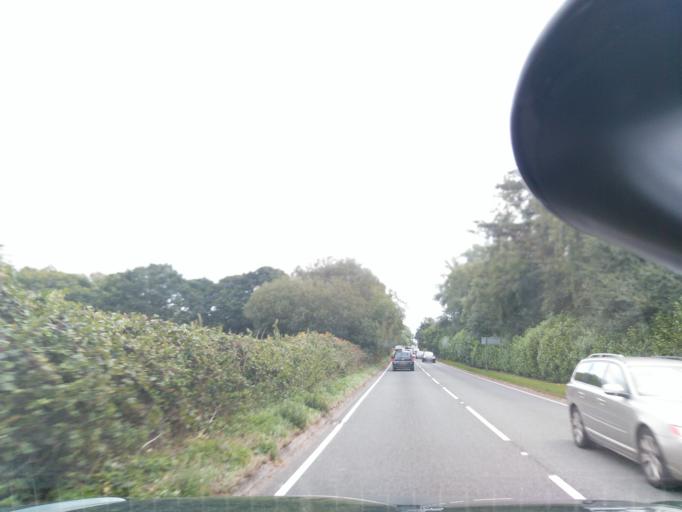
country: GB
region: England
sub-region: Dorset
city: Lytchett Matravers
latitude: 50.7390
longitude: -2.1001
